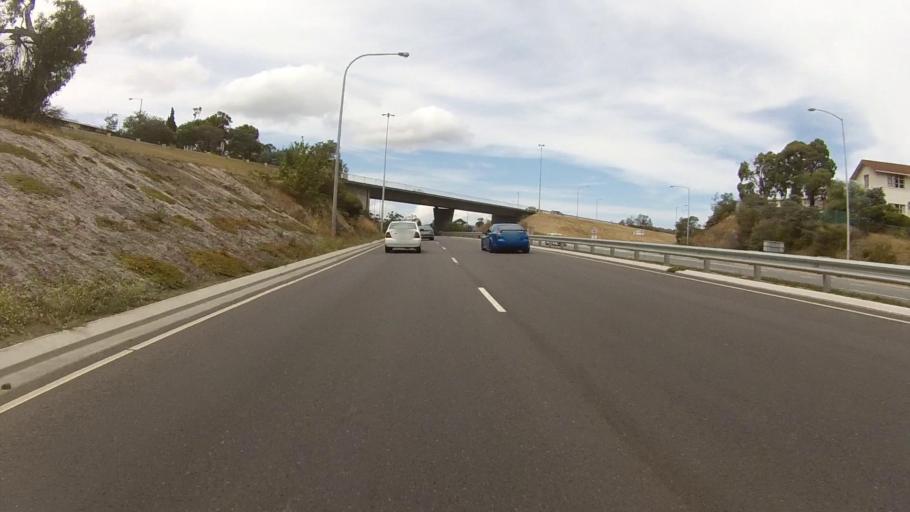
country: AU
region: Tasmania
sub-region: Clarence
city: Lindisfarne
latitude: -42.8625
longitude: 147.3617
